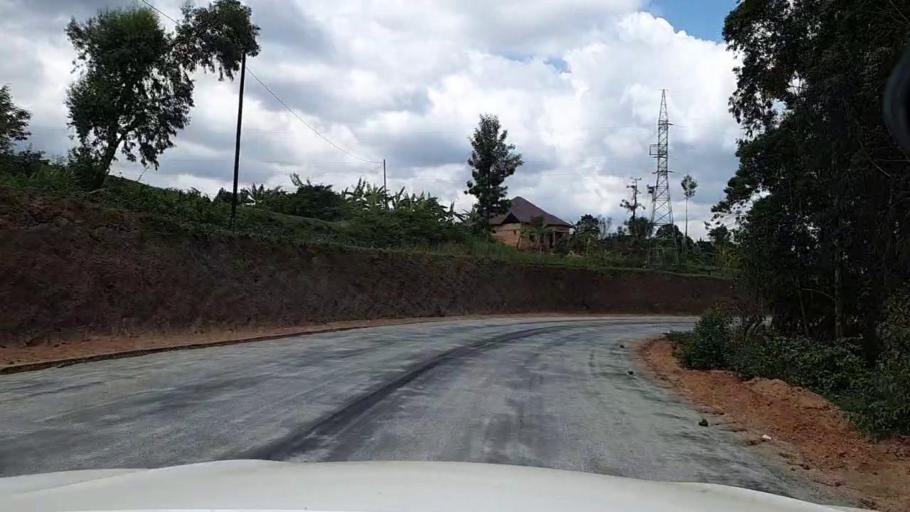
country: RW
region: Southern Province
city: Butare
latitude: -2.6990
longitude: 29.5689
